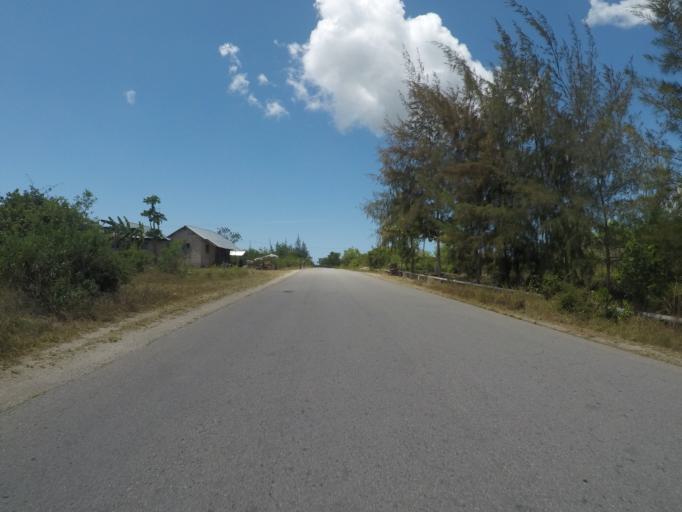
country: TZ
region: Zanzibar Central/South
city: Nganane
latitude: -6.2825
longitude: 39.4695
